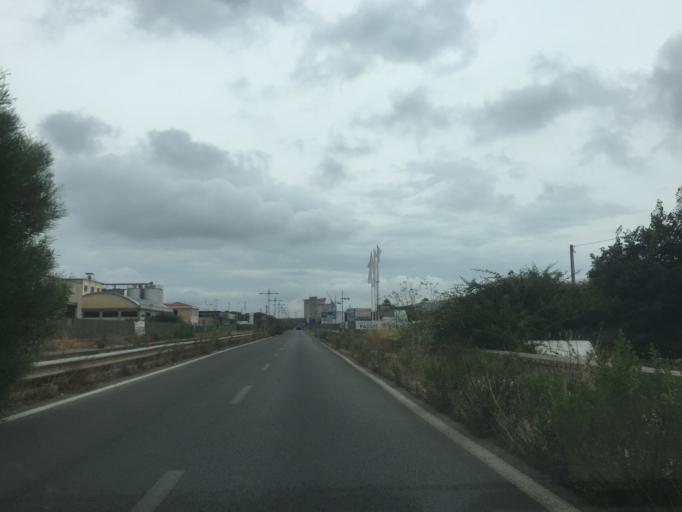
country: IT
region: Sicily
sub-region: Ragusa
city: Ragusa
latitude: 36.8877
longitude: 14.6895
